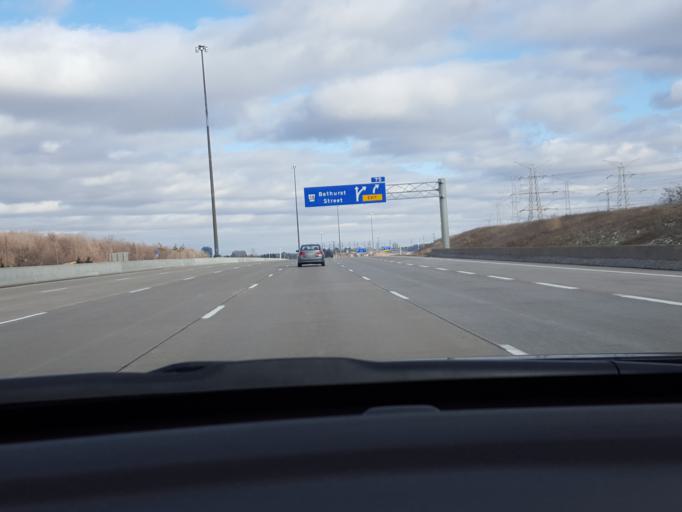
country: CA
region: Ontario
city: Concord
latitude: 43.8243
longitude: -79.4658
